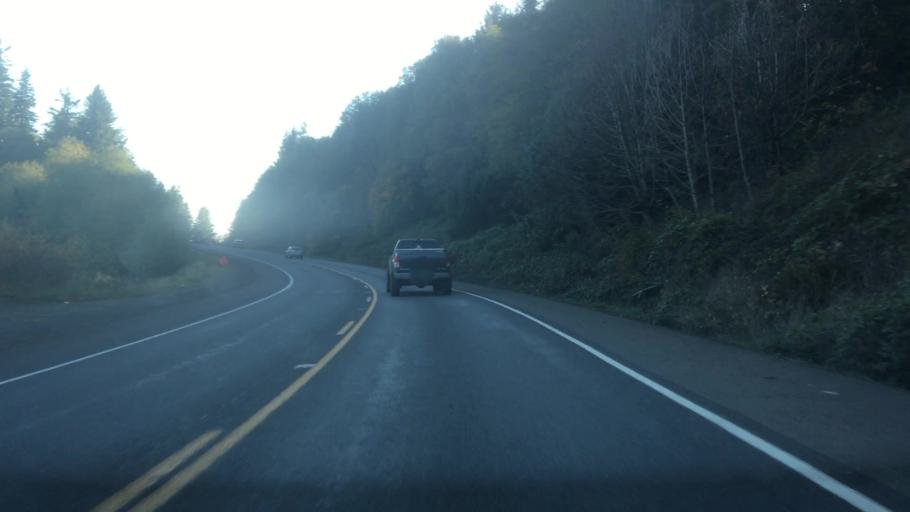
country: US
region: Oregon
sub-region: Clatsop County
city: Astoria
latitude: 46.2588
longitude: -123.8530
